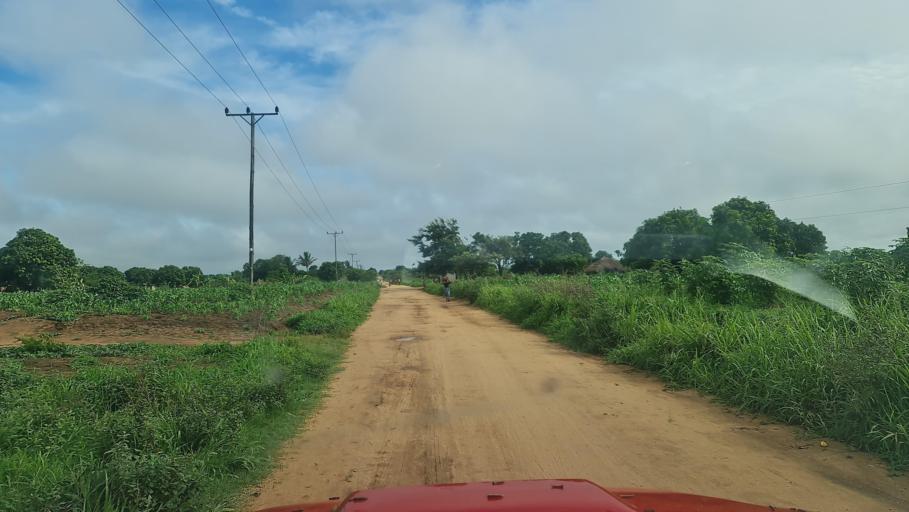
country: MW
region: Southern Region
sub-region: Nsanje District
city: Nsanje
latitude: -17.3118
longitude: 35.5926
